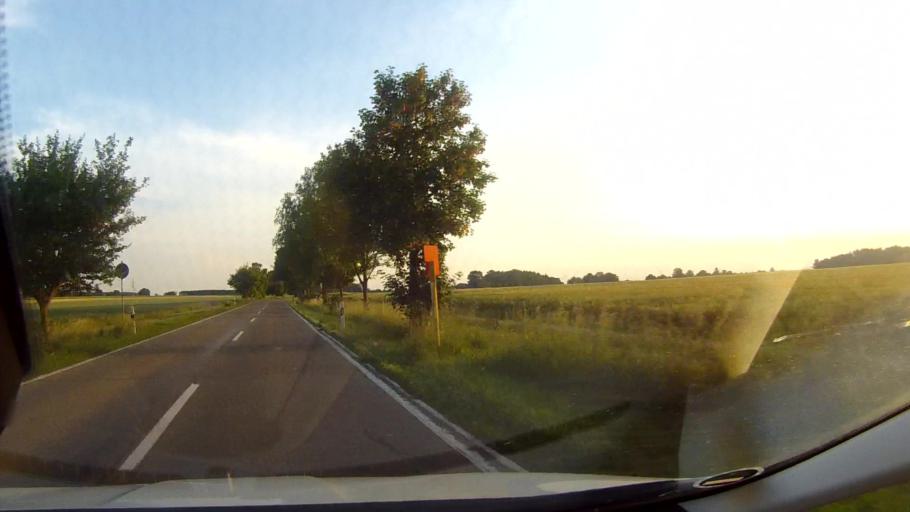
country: DE
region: Baden-Wuerttemberg
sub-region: Tuebingen Region
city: Huttisheim
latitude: 48.2816
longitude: 9.9596
